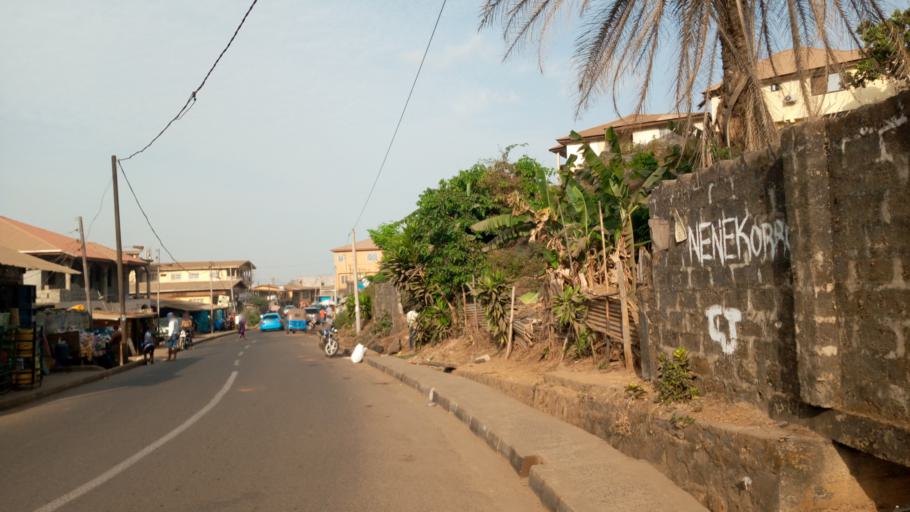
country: SL
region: Western Area
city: Freetown
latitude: 8.4747
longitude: -13.2572
